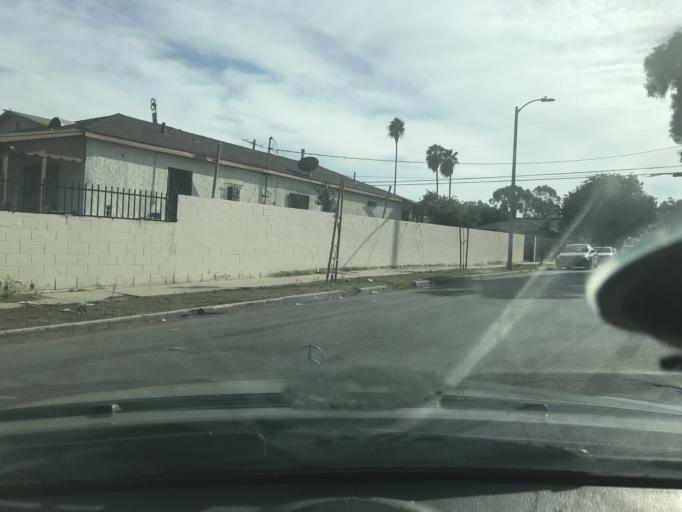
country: US
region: California
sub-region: Los Angeles County
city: Willowbrook
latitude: 33.9301
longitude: -118.2664
